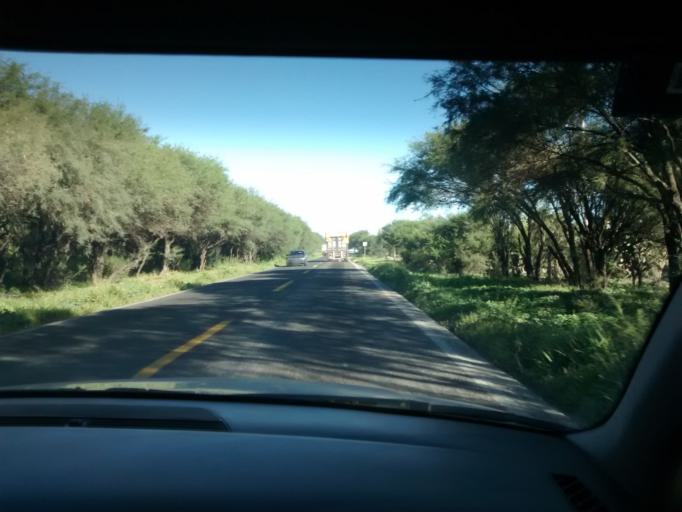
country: MX
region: Puebla
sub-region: Tepanco de Lopez
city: San Andres Cacaloapan
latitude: 18.5498
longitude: -97.5505
